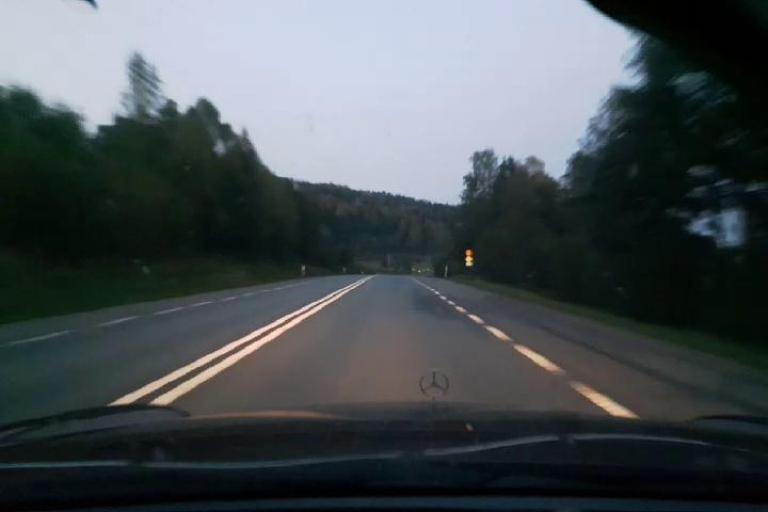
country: SE
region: Vaesternorrland
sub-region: Kramfors Kommun
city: Nordingra
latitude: 63.0079
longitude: 18.2723
